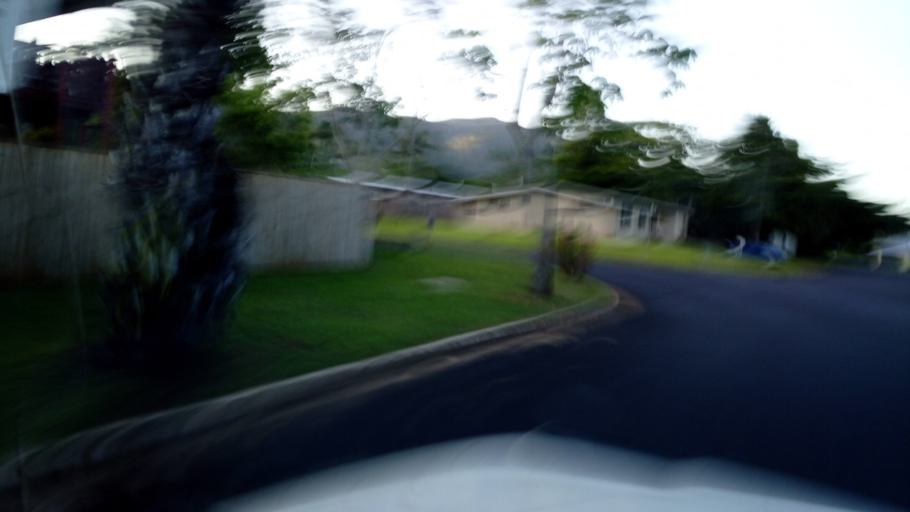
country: AU
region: Queensland
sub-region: Cairns
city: Woree
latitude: -16.9567
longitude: 145.7335
